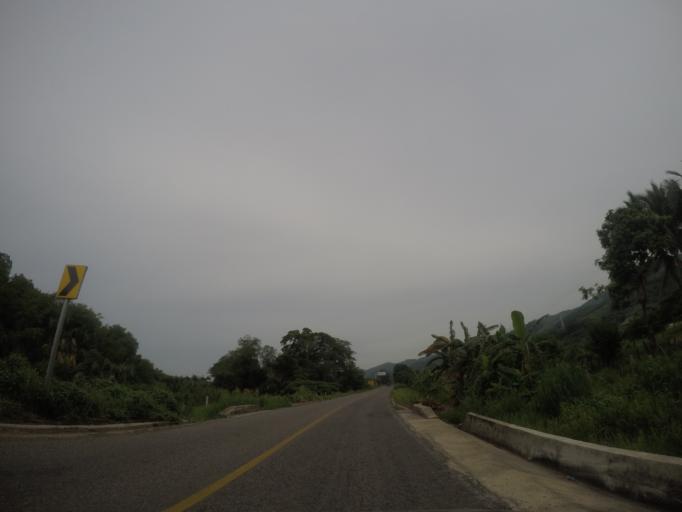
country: MX
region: Oaxaca
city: San Pedro Mixtepec
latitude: 15.9518
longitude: -97.1950
